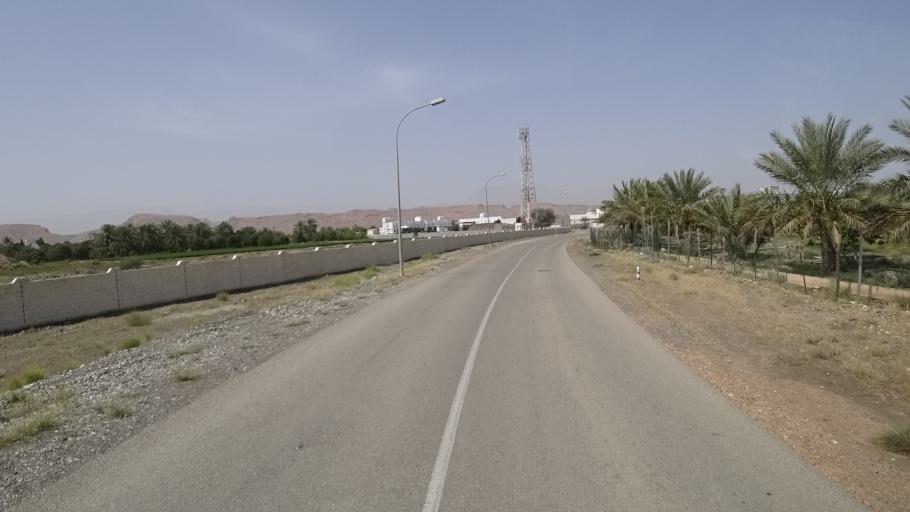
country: OM
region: Muhafazat Masqat
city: Muscat
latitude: 23.2074
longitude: 58.9700
